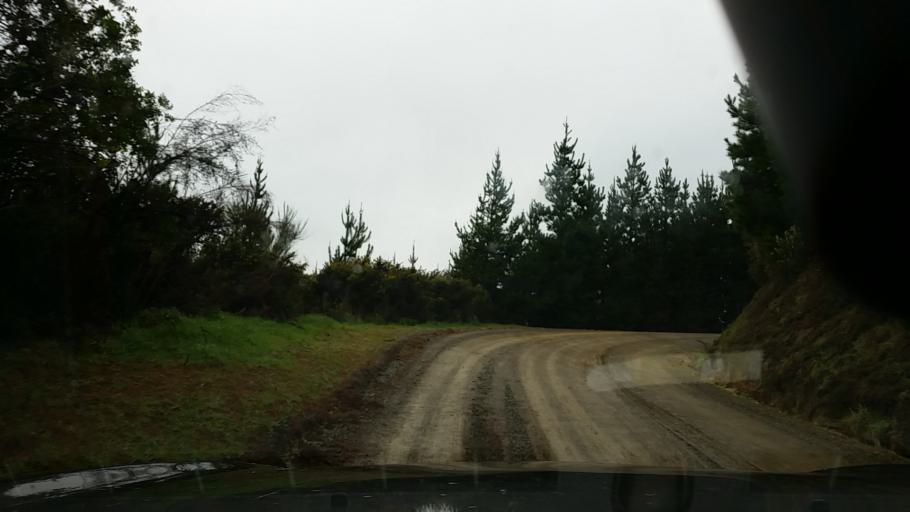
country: NZ
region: Marlborough
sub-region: Marlborough District
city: Picton
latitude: -41.3610
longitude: 174.0714
